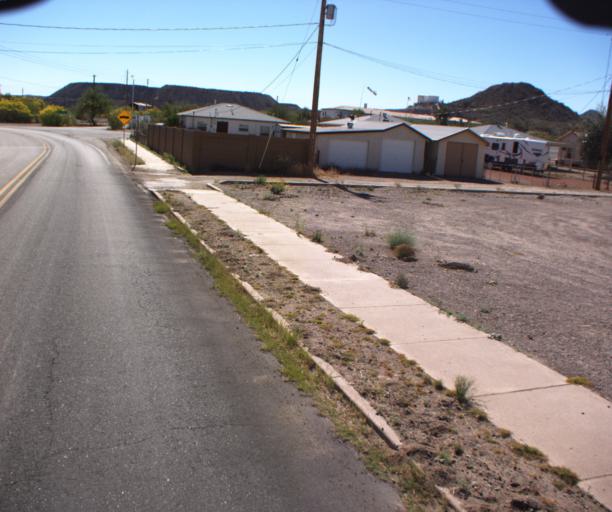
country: US
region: Arizona
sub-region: Pima County
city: Ajo
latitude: 32.3720
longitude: -112.8613
